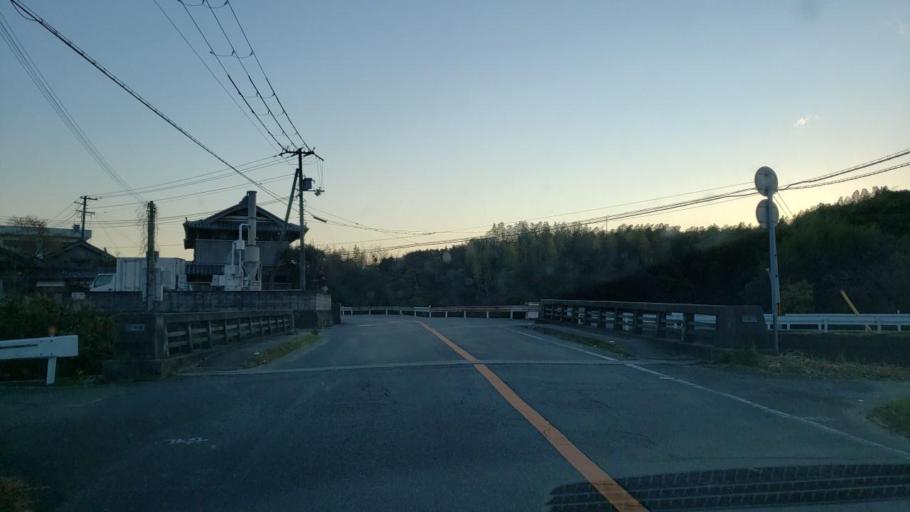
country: JP
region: Hyogo
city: Fukura
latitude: 34.3269
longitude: 134.7727
